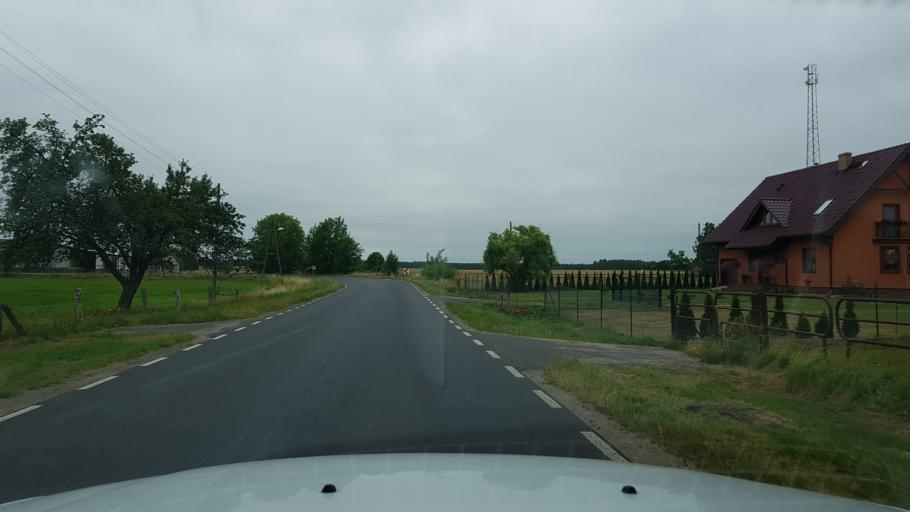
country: PL
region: West Pomeranian Voivodeship
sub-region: Powiat gryficki
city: Brojce
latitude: 53.9405
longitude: 15.4050
